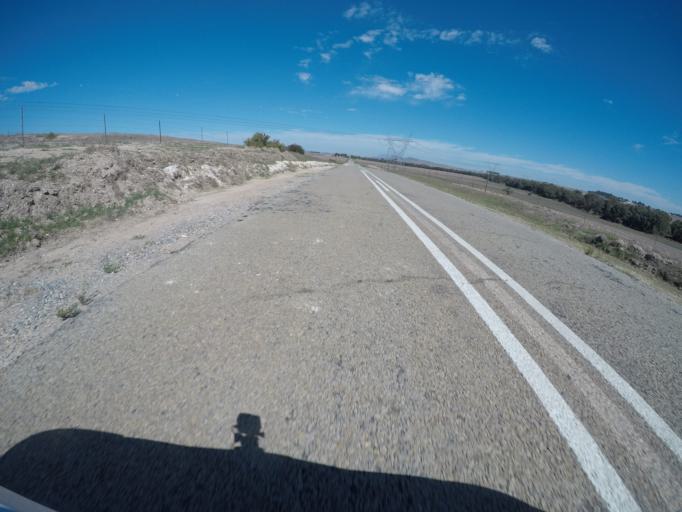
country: ZA
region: Western Cape
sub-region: West Coast District Municipality
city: Malmesbury
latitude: -33.5967
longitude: 18.6432
